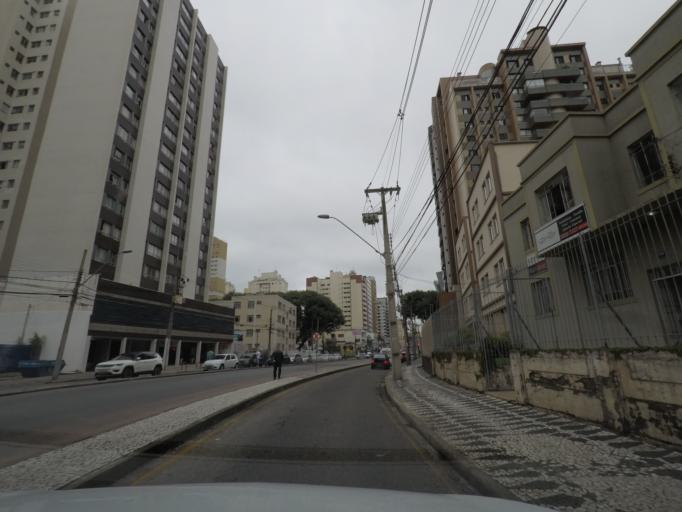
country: BR
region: Parana
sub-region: Curitiba
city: Curitiba
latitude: -25.4529
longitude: -49.2879
